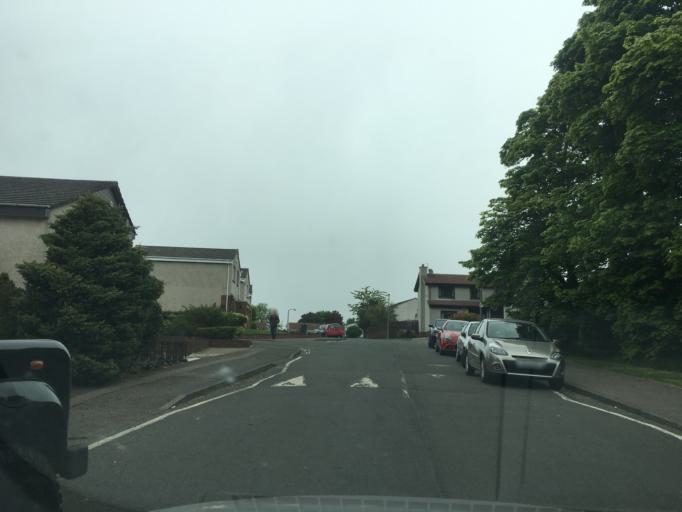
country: GB
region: Scotland
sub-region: Midlothian
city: Loanhead
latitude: 55.9045
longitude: -3.1974
